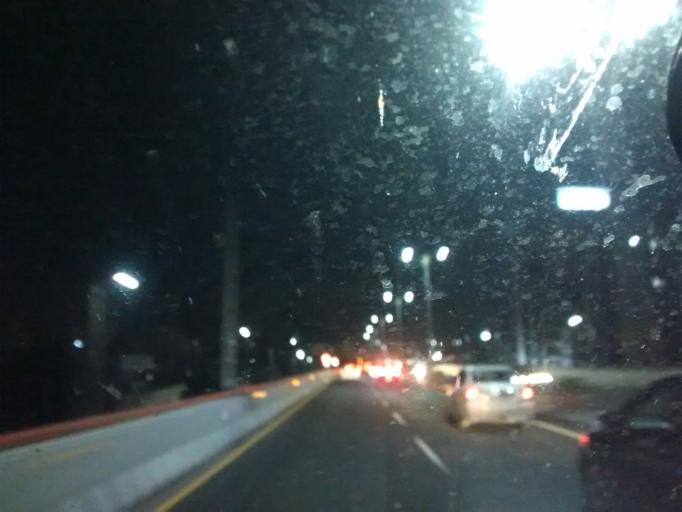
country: IN
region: Telangana
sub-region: Hyderabad
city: Hyderabad
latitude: 17.3495
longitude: 78.4169
